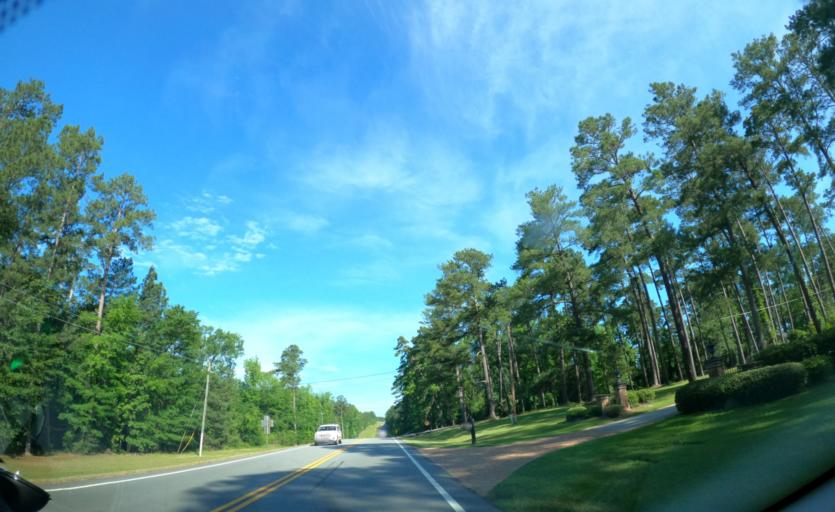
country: US
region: Georgia
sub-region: Columbia County
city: Appling
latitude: 33.6230
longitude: -82.2794
